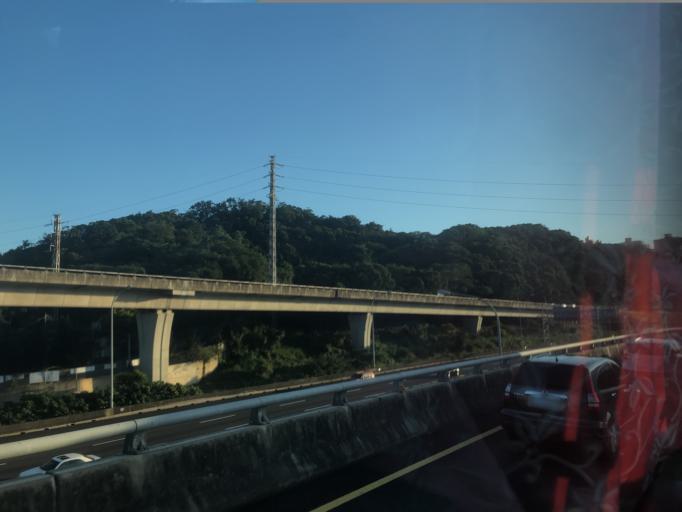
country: TW
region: Taiwan
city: Daxi
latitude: 24.9053
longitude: 121.1619
